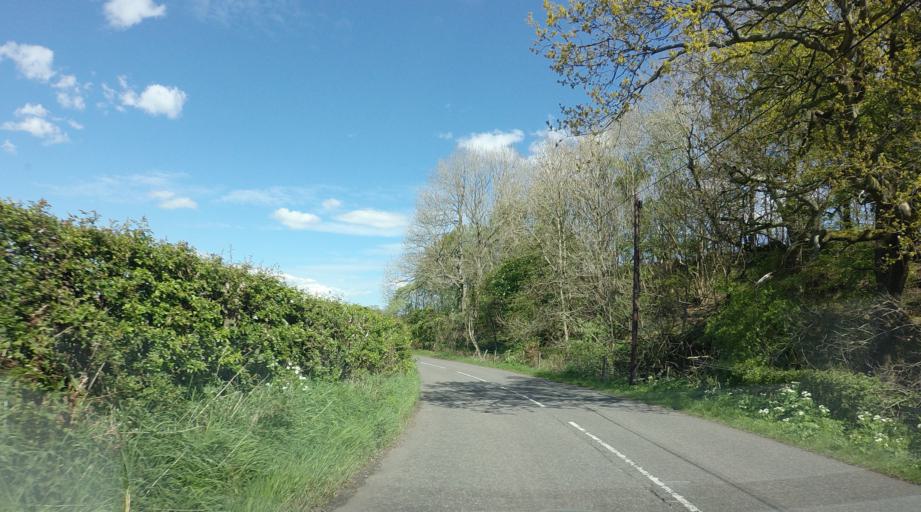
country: GB
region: Scotland
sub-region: Falkirk
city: Polmont
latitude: 55.9700
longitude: -3.6580
